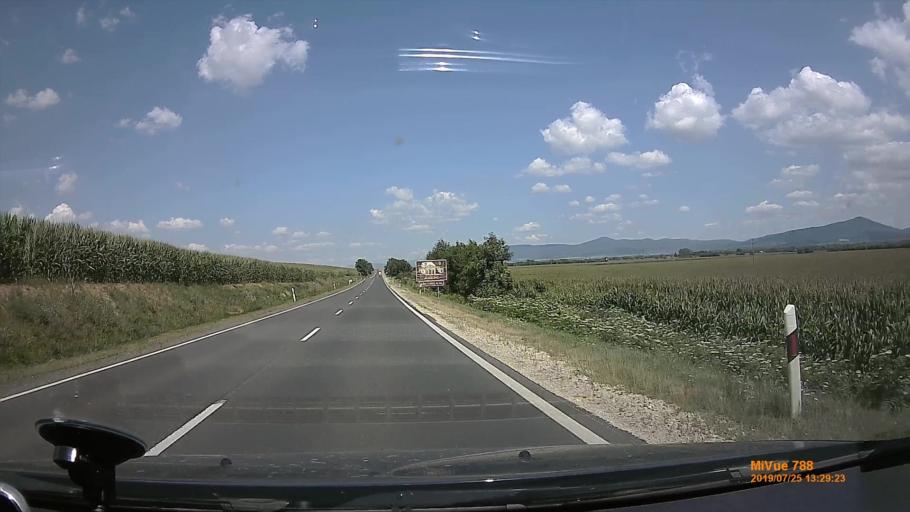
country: HU
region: Borsod-Abauj-Zemplen
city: Encs
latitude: 48.3424
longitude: 21.1157
